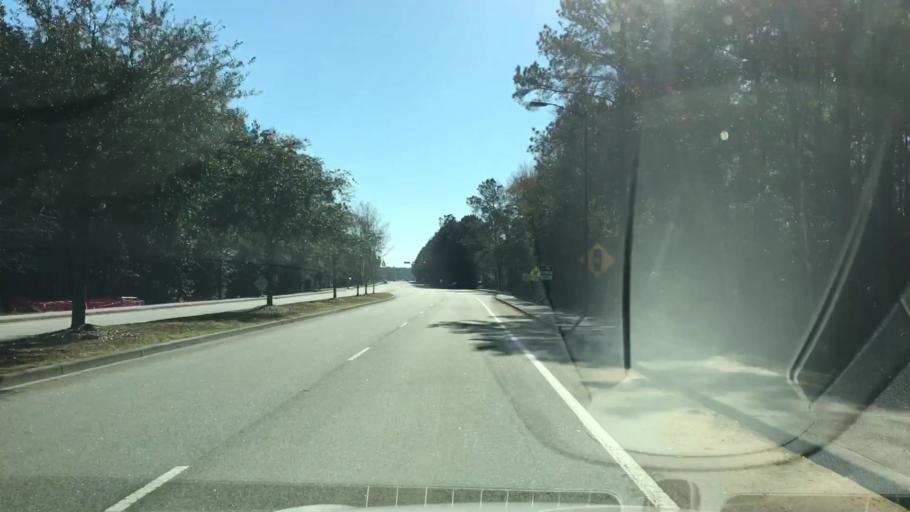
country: US
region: South Carolina
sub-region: Berkeley County
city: Ladson
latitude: 32.9232
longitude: -80.1112
